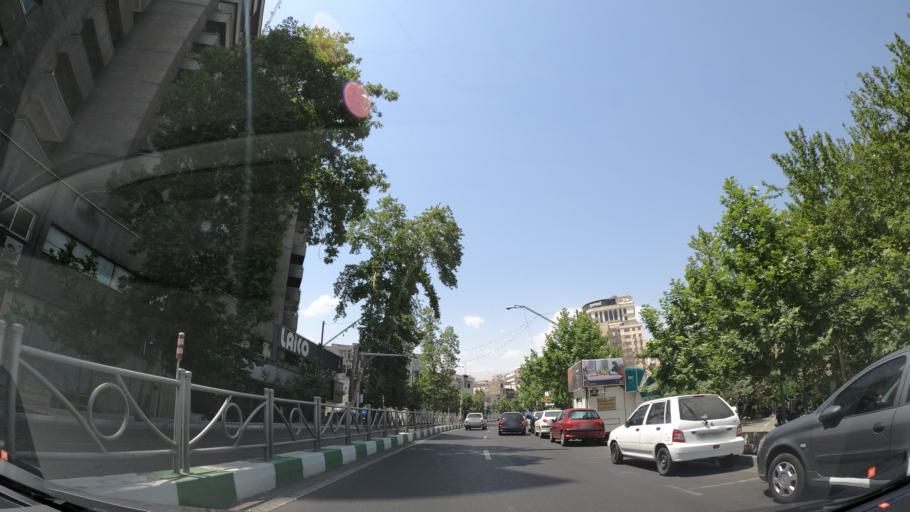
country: IR
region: Tehran
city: Tehran
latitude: 35.7373
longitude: 51.4091
